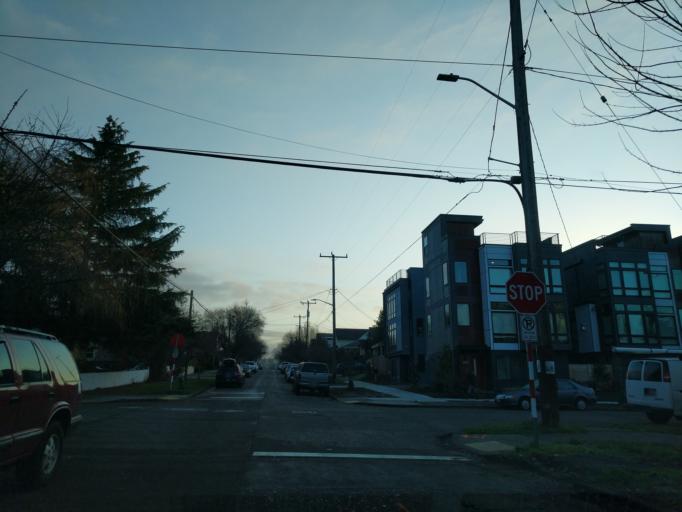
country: US
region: Washington
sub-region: King County
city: Seattle
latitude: 47.6753
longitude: -122.3793
